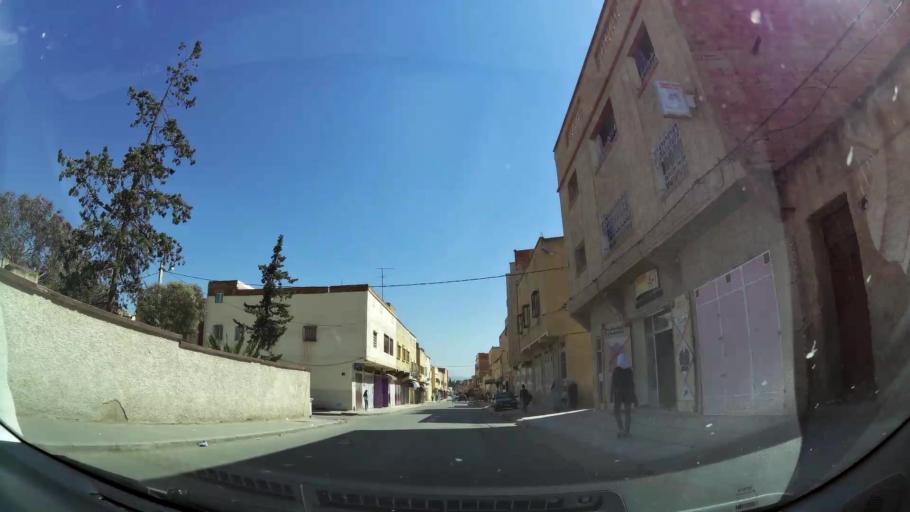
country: MA
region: Oriental
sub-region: Oujda-Angad
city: Oujda
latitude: 34.6829
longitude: -1.9321
